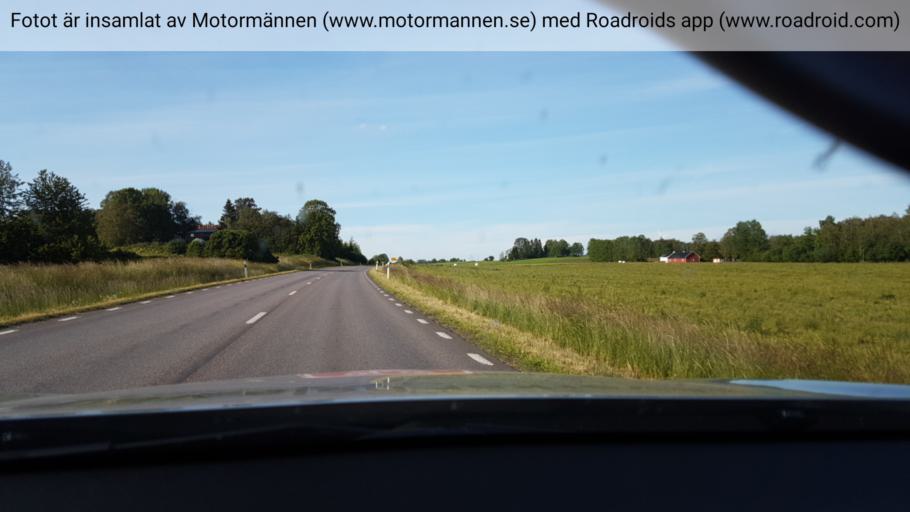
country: SE
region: Vaestra Goetaland
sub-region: Falkopings Kommun
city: Falkoeping
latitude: 58.0986
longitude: 13.5288
